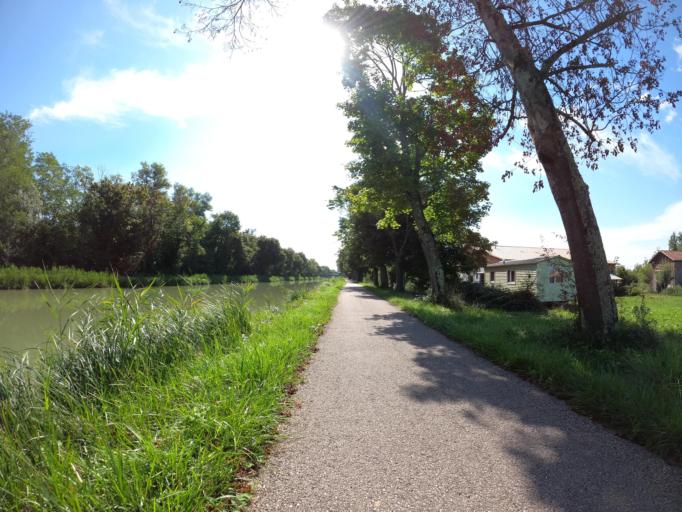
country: FR
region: Midi-Pyrenees
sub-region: Departement du Tarn-et-Garonne
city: Montech
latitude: 43.9371
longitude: 1.2532
